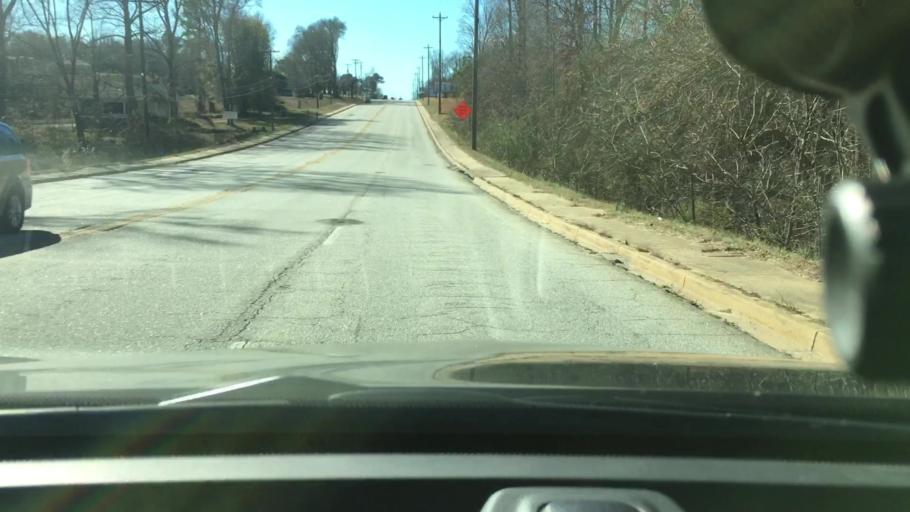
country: US
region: South Carolina
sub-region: Cherokee County
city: East Gaffney
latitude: 35.0994
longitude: -81.6283
